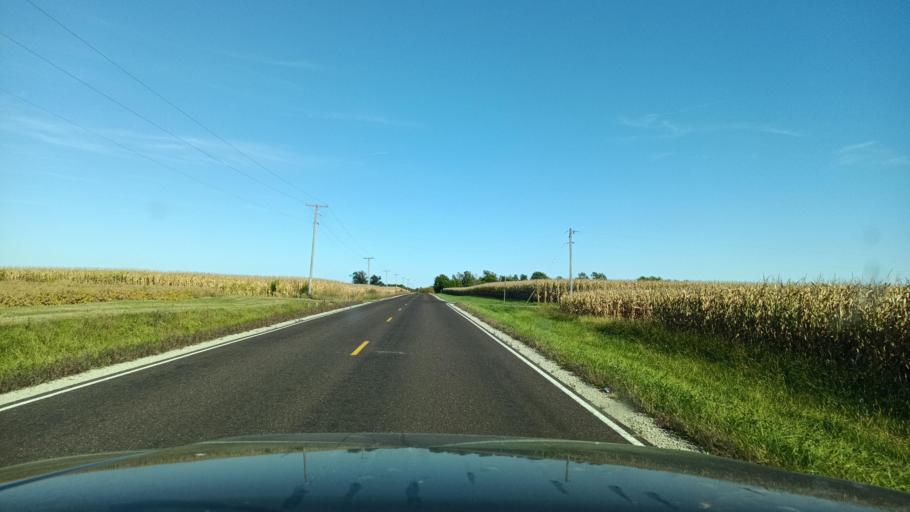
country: US
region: Illinois
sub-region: McLean County
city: Heyworth
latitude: 40.2386
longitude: -89.0920
